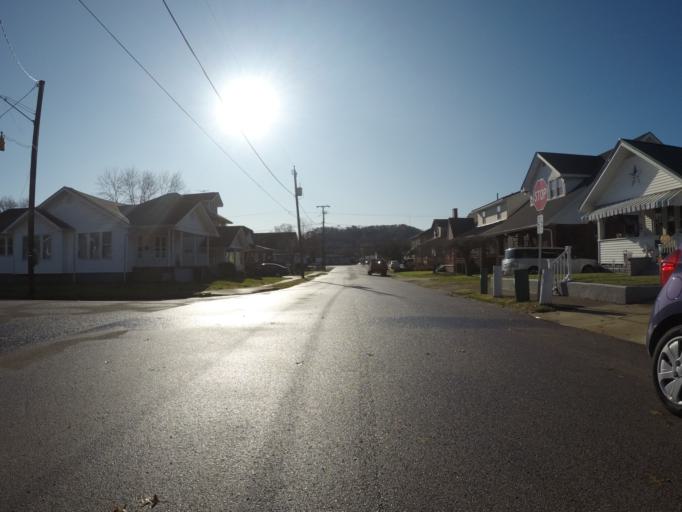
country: US
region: Ohio
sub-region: Lawrence County
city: Burlington
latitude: 38.4090
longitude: -82.4953
